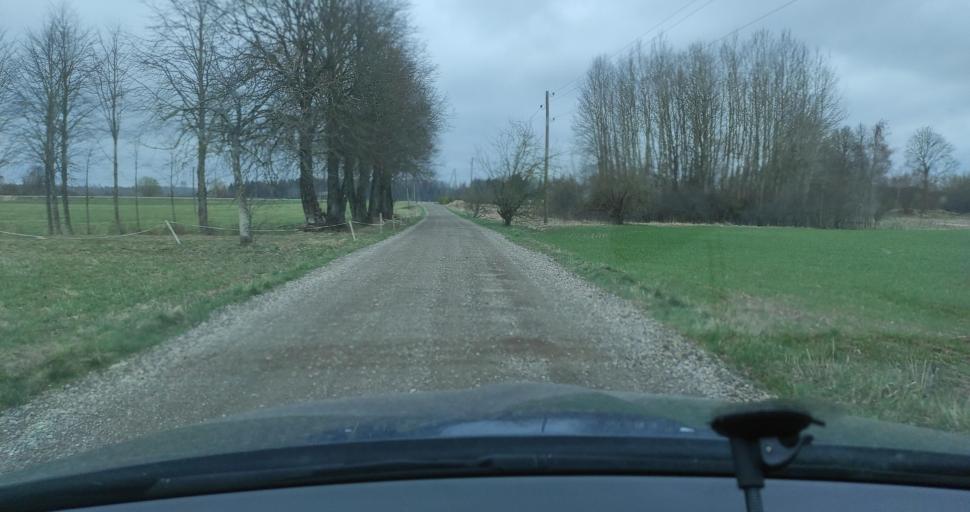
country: LV
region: Saldus Rajons
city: Saldus
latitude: 56.6312
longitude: 22.4264
